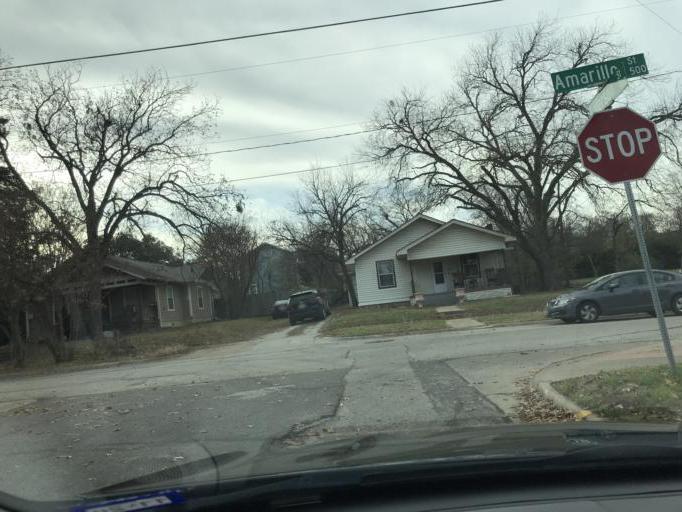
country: US
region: Texas
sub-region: Denton County
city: Denton
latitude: 33.2165
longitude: -97.1425
